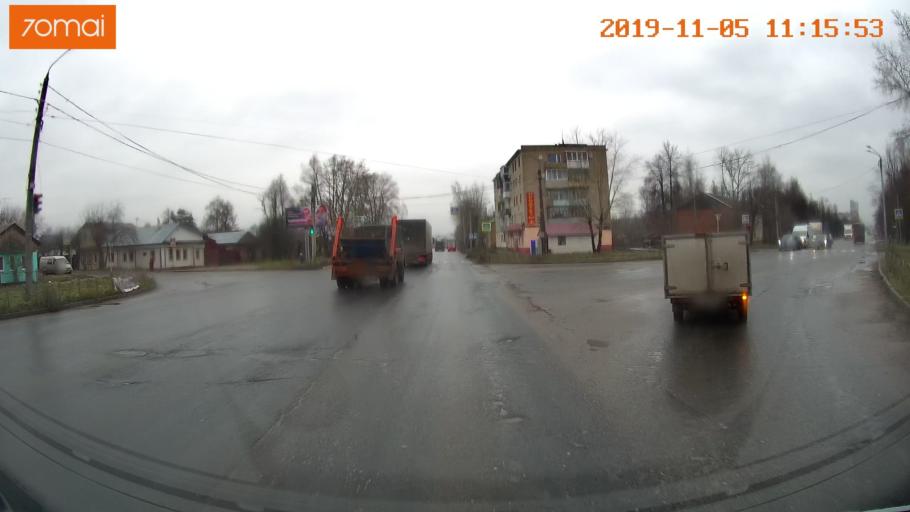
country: RU
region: Ivanovo
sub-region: Gorod Ivanovo
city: Ivanovo
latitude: 56.9804
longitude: 40.9538
